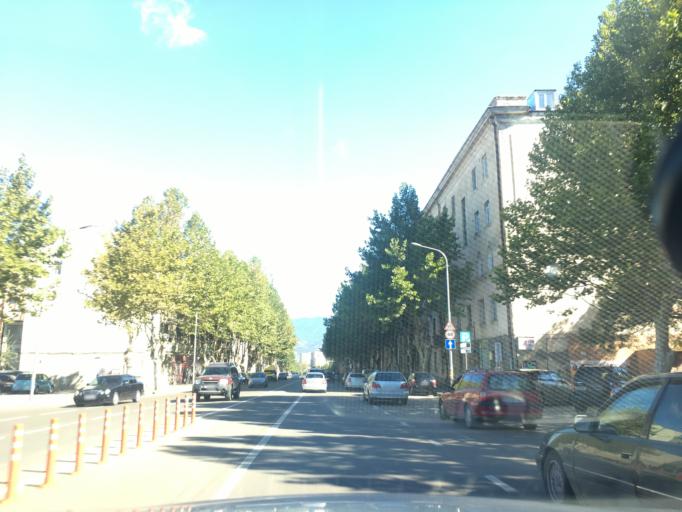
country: GE
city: Zahesi
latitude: 41.7700
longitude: 44.7927
